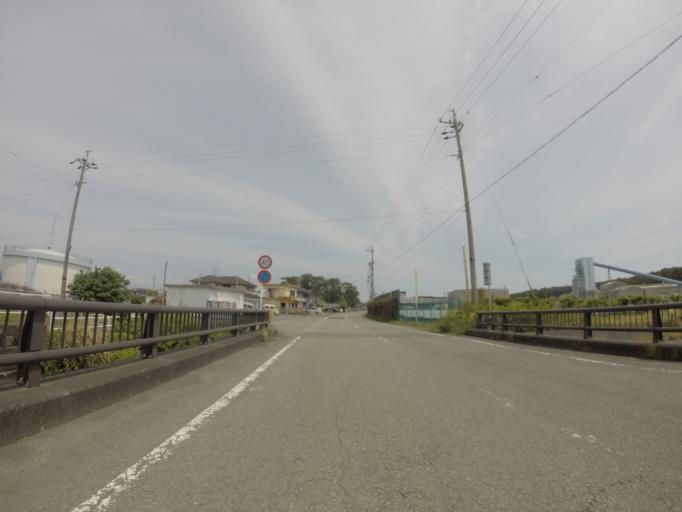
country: JP
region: Shizuoka
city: Yaizu
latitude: 34.7850
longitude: 138.2998
